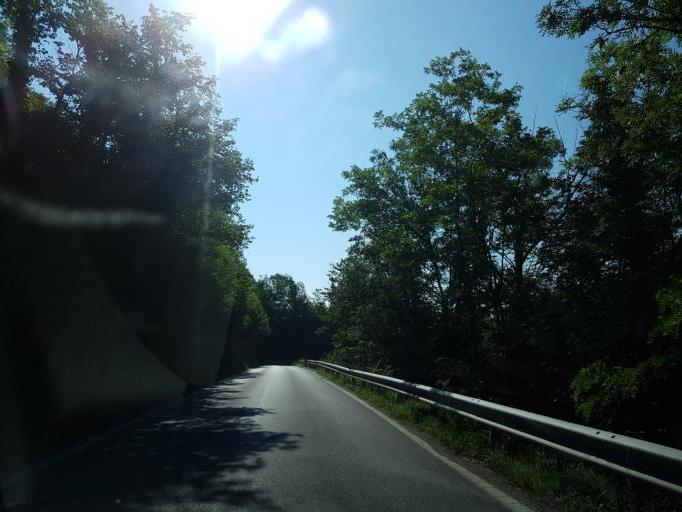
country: IT
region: Piedmont
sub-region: Provincia di Cuneo
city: San Damiano Macra
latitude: 44.4882
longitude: 7.2640
